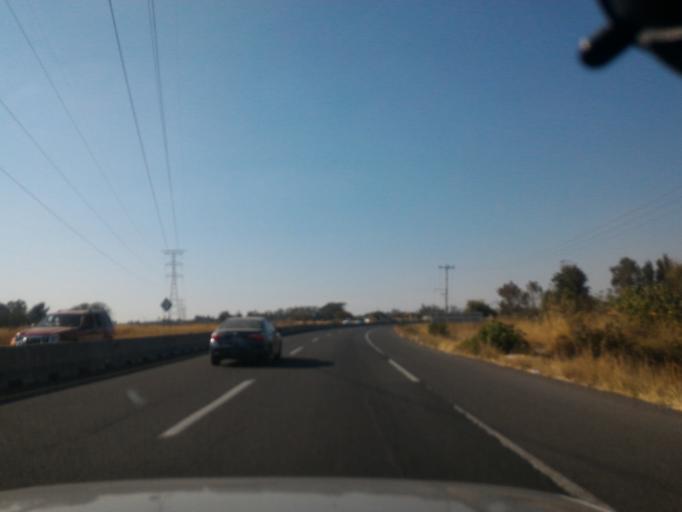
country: MX
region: Jalisco
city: Atequiza
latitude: 20.3961
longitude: -103.1465
